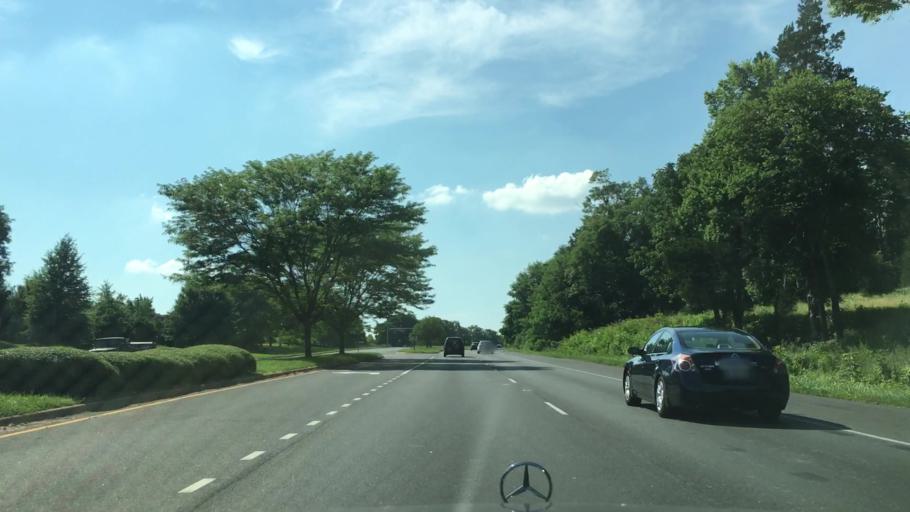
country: US
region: Virginia
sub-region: City of Charlottesville
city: Charlottesville
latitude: 38.0249
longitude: -78.4361
